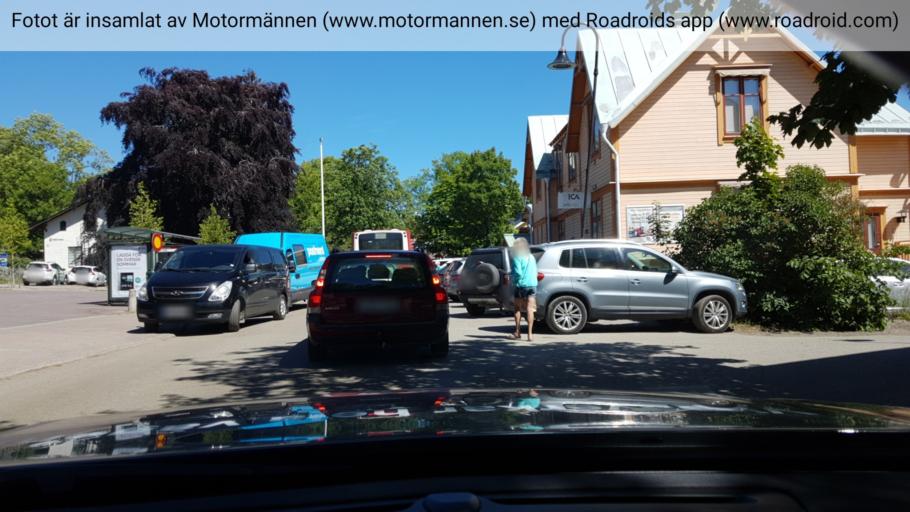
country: SE
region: Stockholm
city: Dalaro
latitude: 59.1334
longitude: 18.4084
